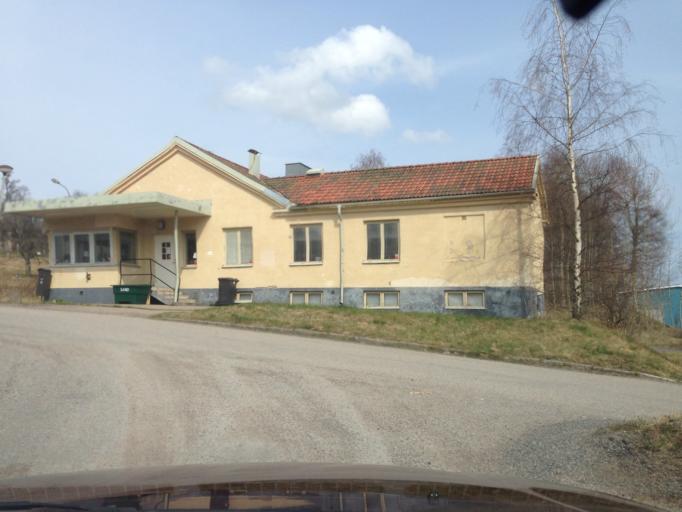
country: SE
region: Dalarna
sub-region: Ludvika Kommun
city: Grangesberg
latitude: 60.0769
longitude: 14.9875
